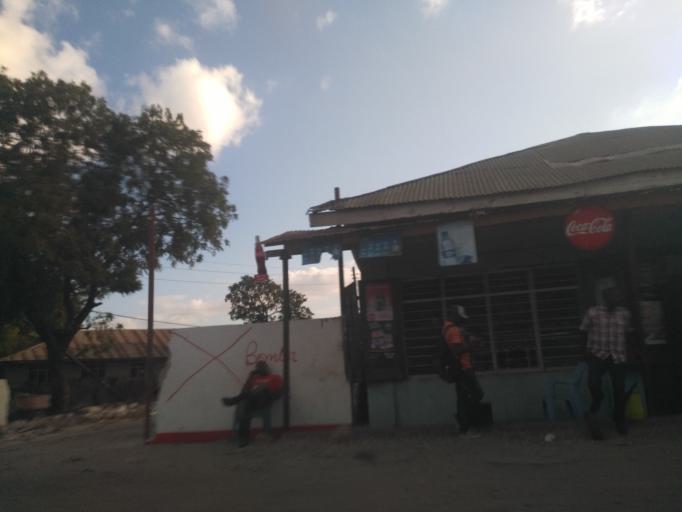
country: TZ
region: Dar es Salaam
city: Dar es Salaam
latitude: -6.8508
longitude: 39.2608
